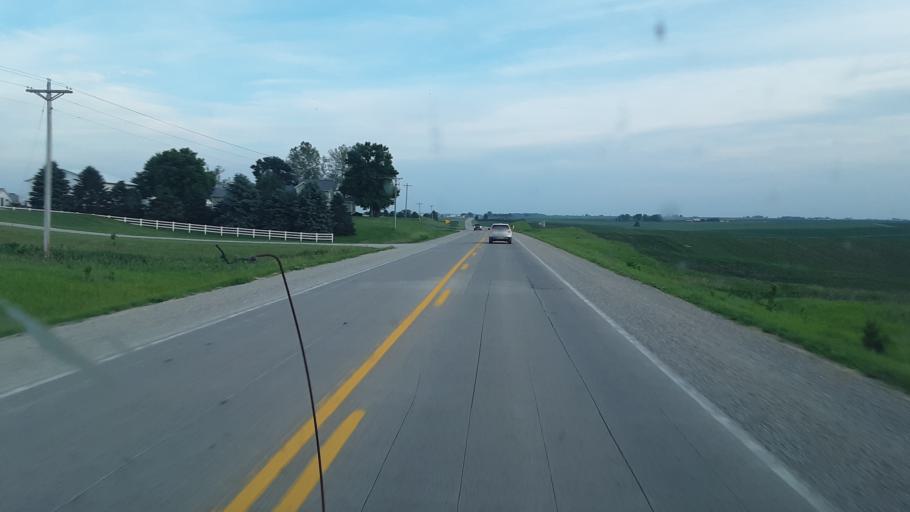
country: US
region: Iowa
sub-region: Benton County
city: Belle Plaine
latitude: 41.8167
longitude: -92.2789
